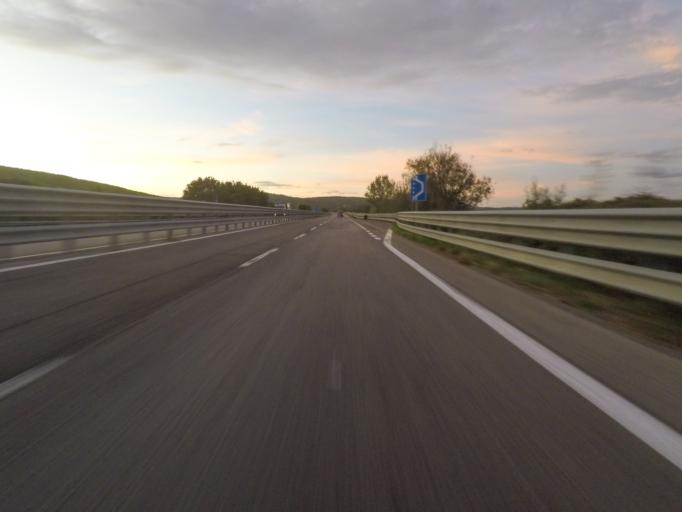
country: IT
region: Tuscany
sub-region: Province of Arezzo
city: Lucignano
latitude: 43.2483
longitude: 11.7183
